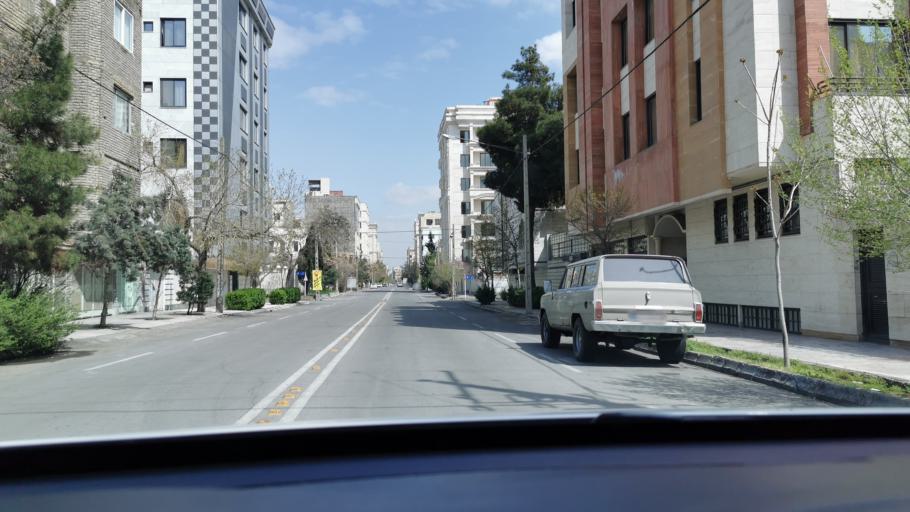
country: IR
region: Razavi Khorasan
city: Mashhad
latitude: 36.3212
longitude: 59.5308
